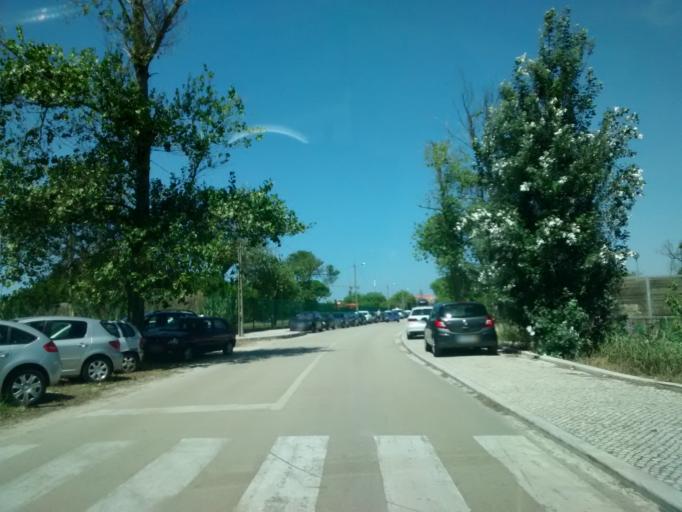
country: PT
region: Coimbra
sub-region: Mira
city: Mira
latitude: 40.4471
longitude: -8.7999
